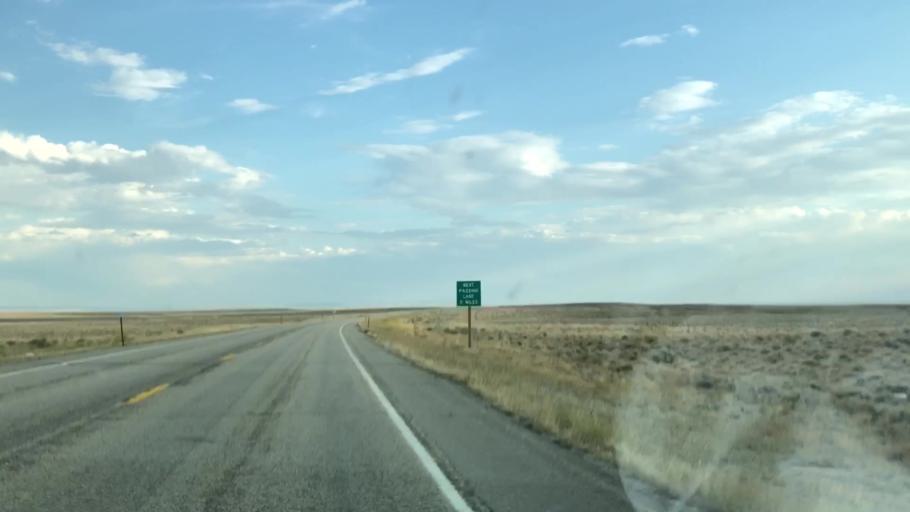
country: US
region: Wyoming
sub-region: Sweetwater County
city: North Rock Springs
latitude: 42.2578
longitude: -109.4701
